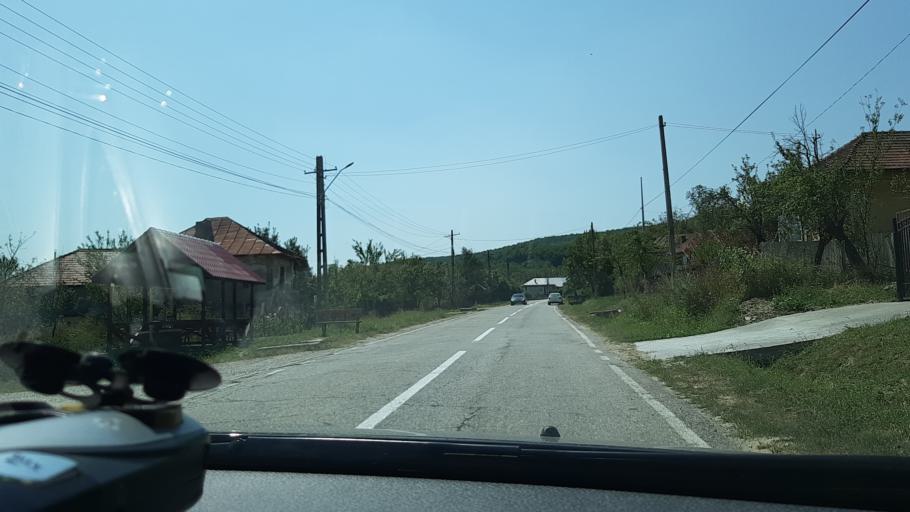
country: RO
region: Gorj
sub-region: Comuna Hurezani
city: Hurezani
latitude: 44.8412
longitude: 23.6395
